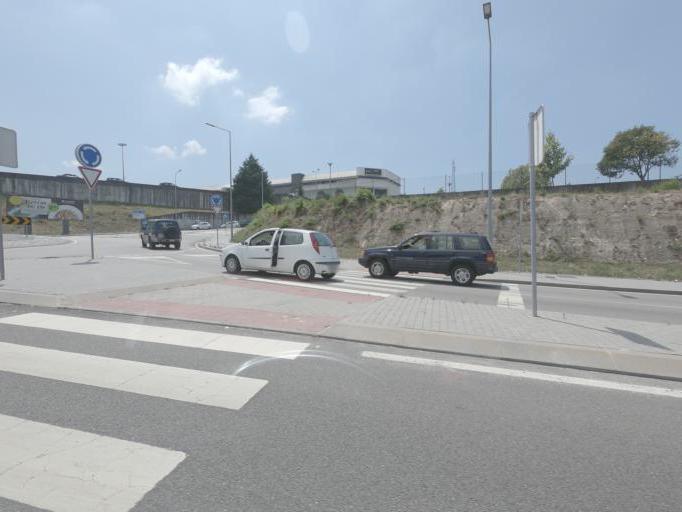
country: PT
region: Porto
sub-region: Penafiel
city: Penafiel
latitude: 41.1955
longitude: -8.3063
